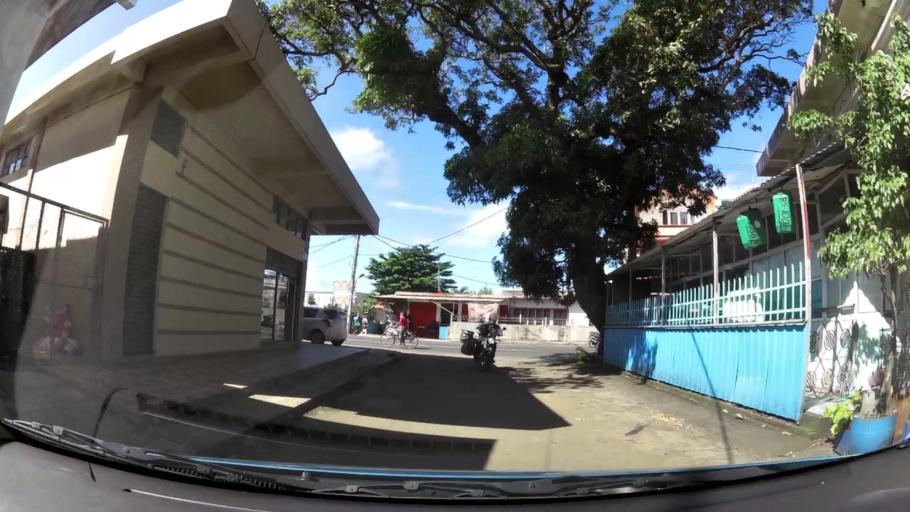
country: MU
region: Grand Port
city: Plaine Magnien
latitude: -20.4308
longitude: 57.6650
